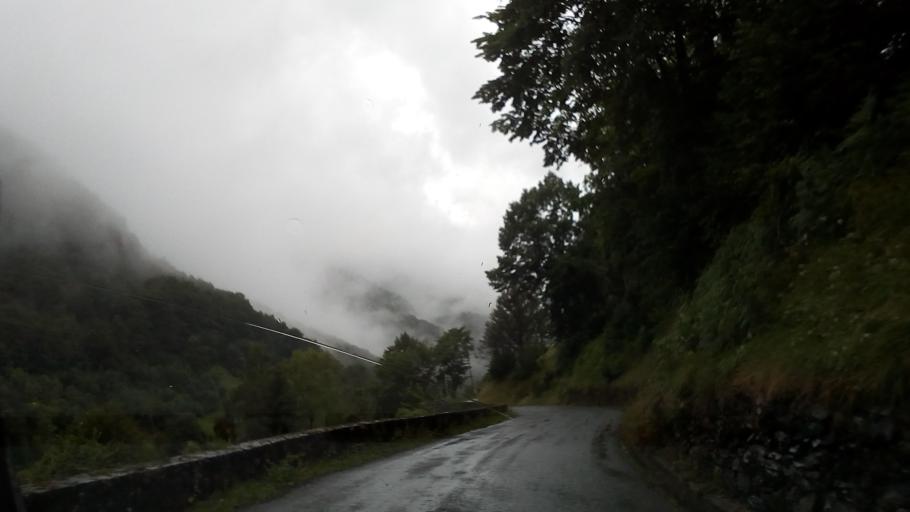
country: FR
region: Midi-Pyrenees
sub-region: Departement des Hautes-Pyrenees
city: Cauterets
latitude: 42.9411
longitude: -0.2315
